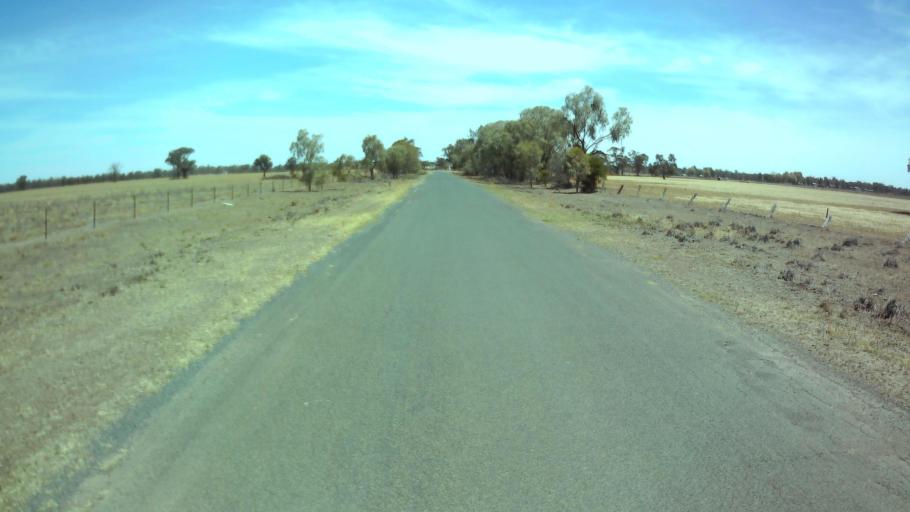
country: AU
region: New South Wales
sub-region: Weddin
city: Grenfell
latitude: -33.8277
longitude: 147.7463
